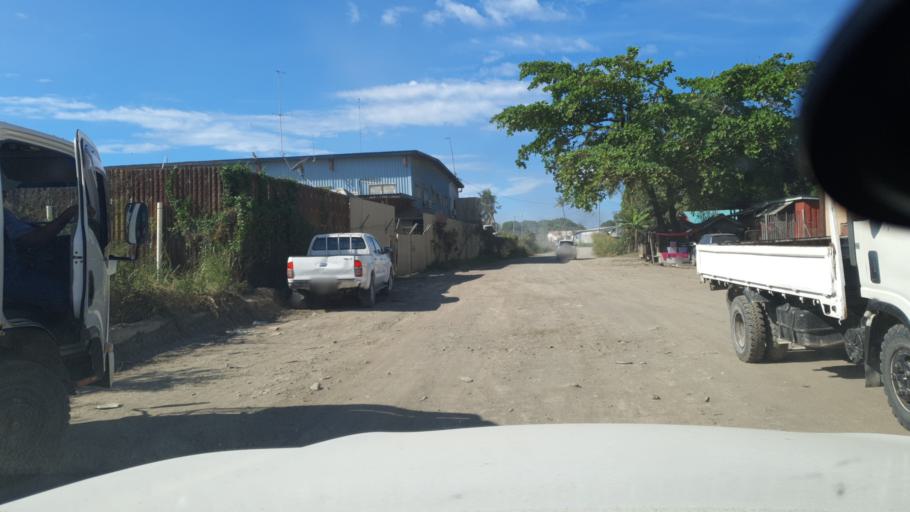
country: SB
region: Guadalcanal
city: Honiara
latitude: -9.4219
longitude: 160.0092
